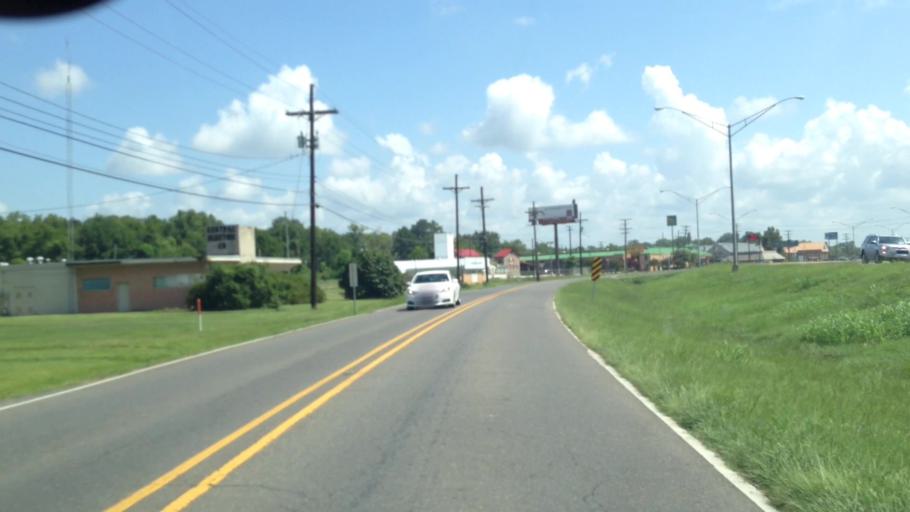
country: US
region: Louisiana
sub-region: Rapides Parish
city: Alexandria
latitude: 31.3077
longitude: -92.4798
